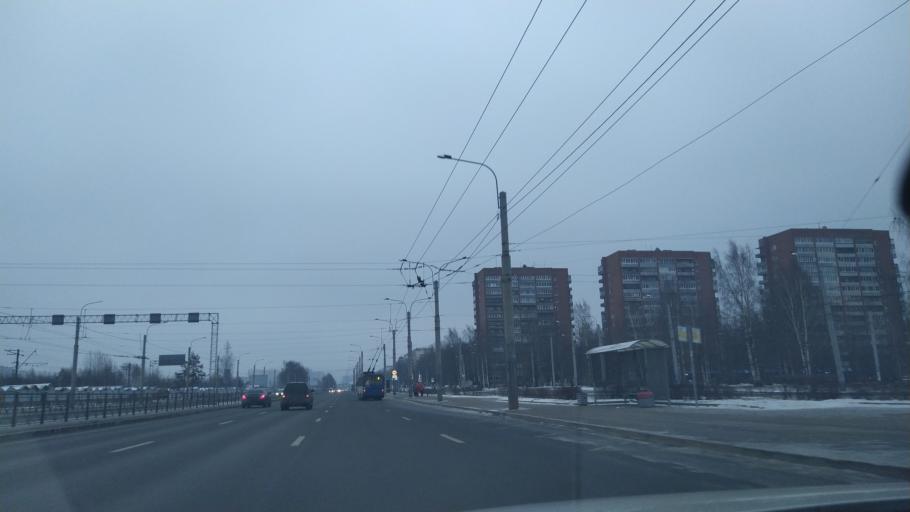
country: RU
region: St.-Petersburg
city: Grazhdanka
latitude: 60.0476
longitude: 30.4059
